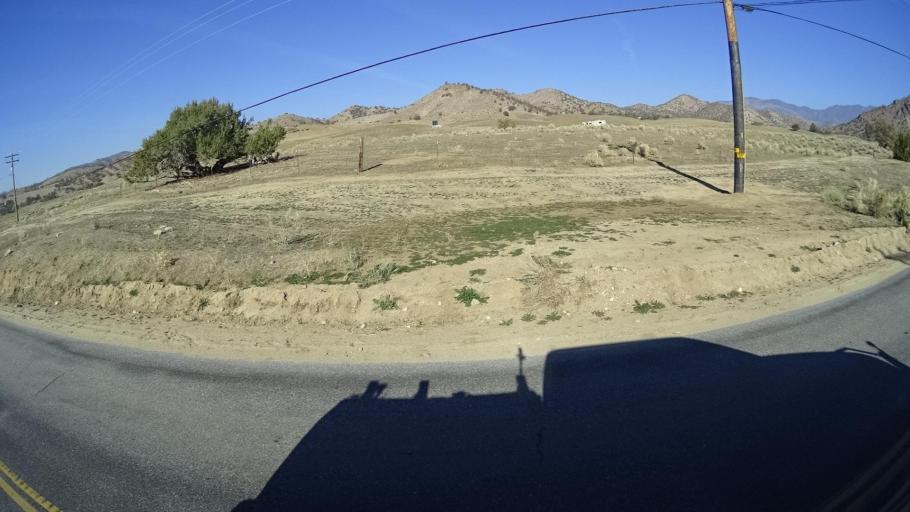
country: US
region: California
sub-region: Kern County
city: Tehachapi
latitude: 35.3183
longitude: -118.3924
